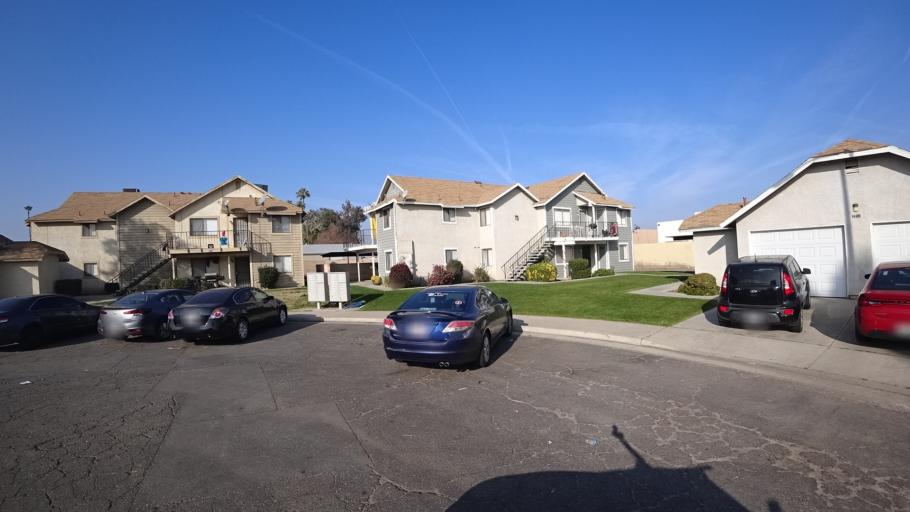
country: US
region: California
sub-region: Kern County
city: Bakersfield
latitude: 35.3301
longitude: -119.0371
